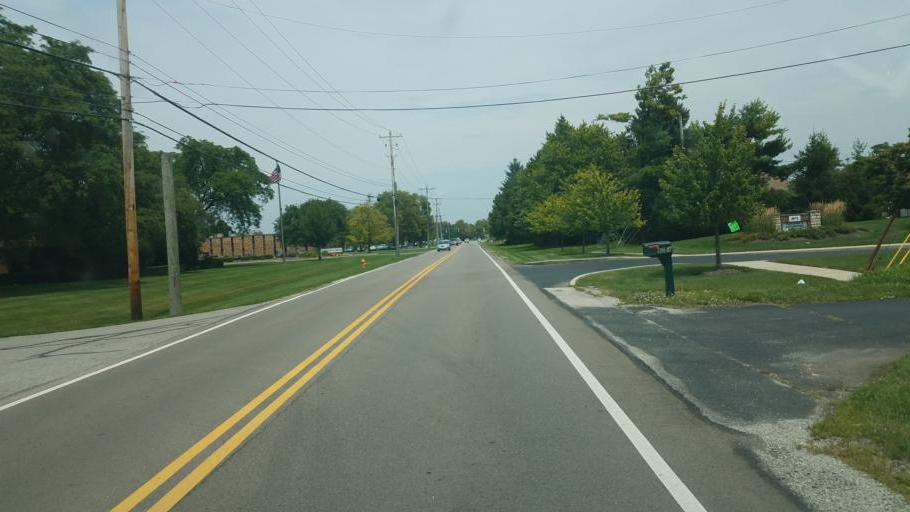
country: US
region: Ohio
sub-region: Franklin County
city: Worthington
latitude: 40.0605
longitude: -83.0666
